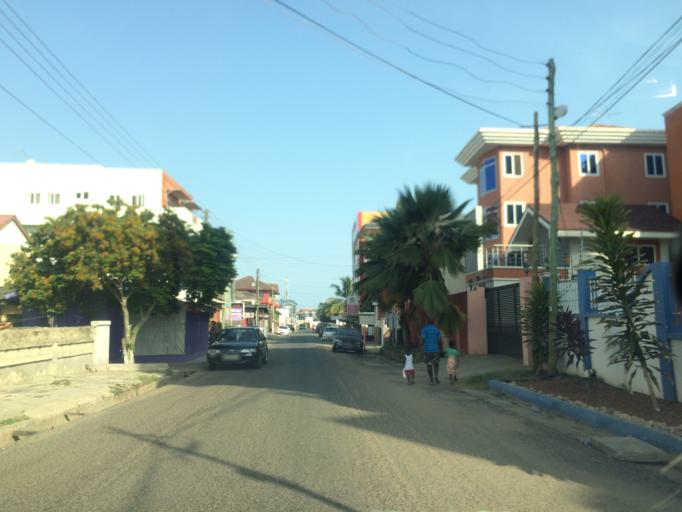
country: GH
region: Greater Accra
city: Accra
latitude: 5.5634
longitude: -0.1844
